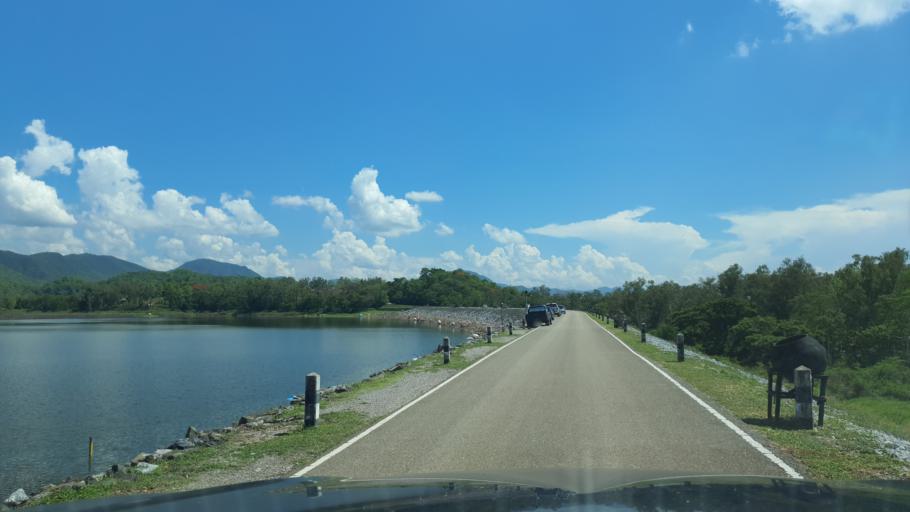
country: TH
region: Chiang Mai
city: Mae On
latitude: 18.8111
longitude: 99.2653
